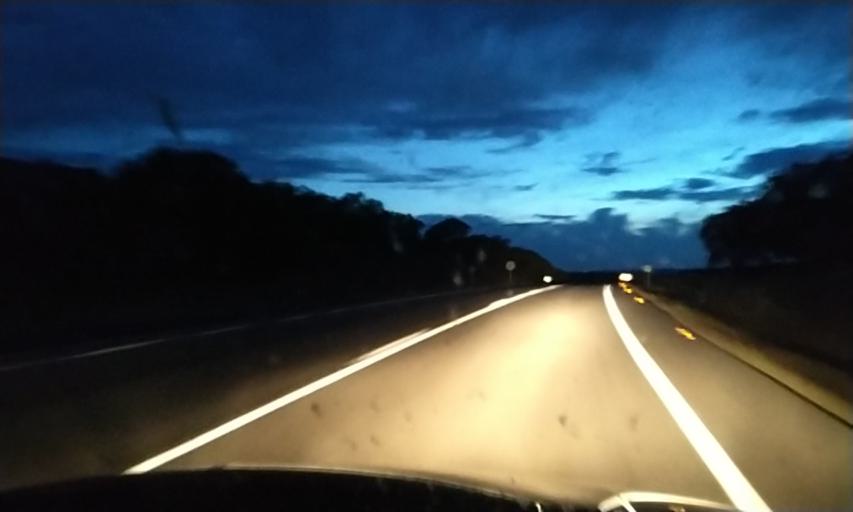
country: ES
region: Extremadura
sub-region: Provincia de Caceres
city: Carcaboso
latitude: 39.9818
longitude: -6.1821
